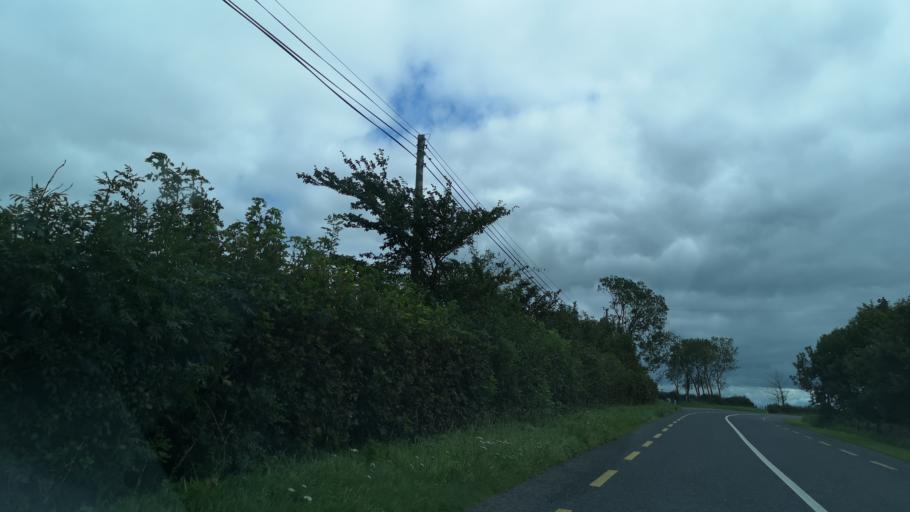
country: IE
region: Connaught
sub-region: County Galway
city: Ballinasloe
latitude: 53.3184
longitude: -8.1741
